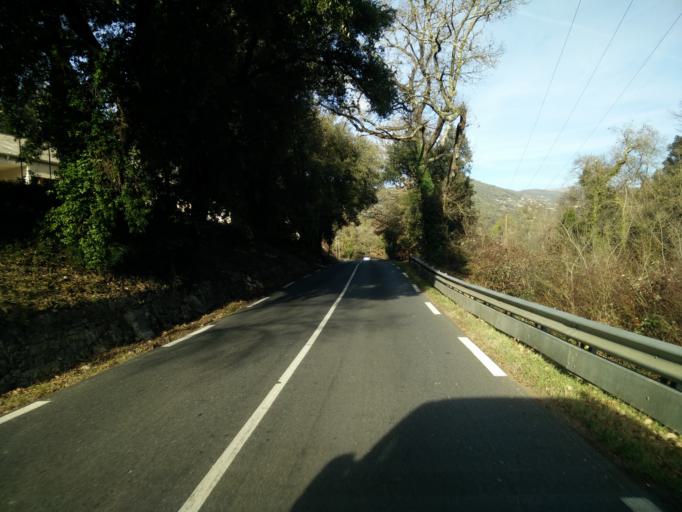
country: FR
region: Provence-Alpes-Cote d'Azur
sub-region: Departement des Alpes-Maritimes
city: Le Tignet
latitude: 43.6147
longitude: 6.8210
